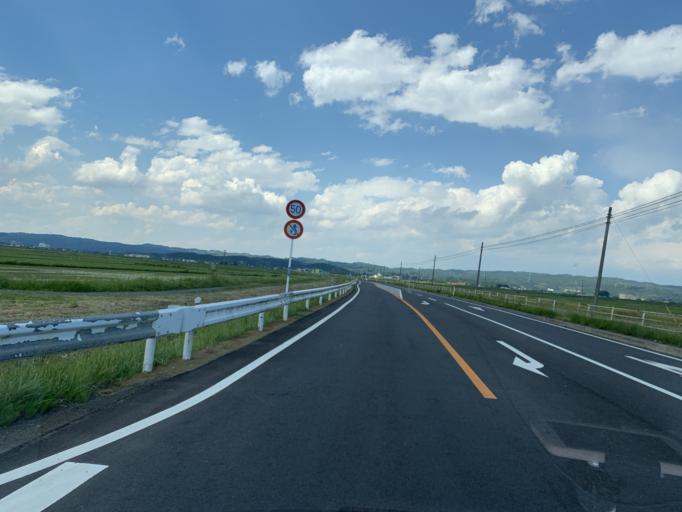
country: JP
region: Miyagi
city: Wakuya
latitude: 38.5190
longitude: 141.1284
